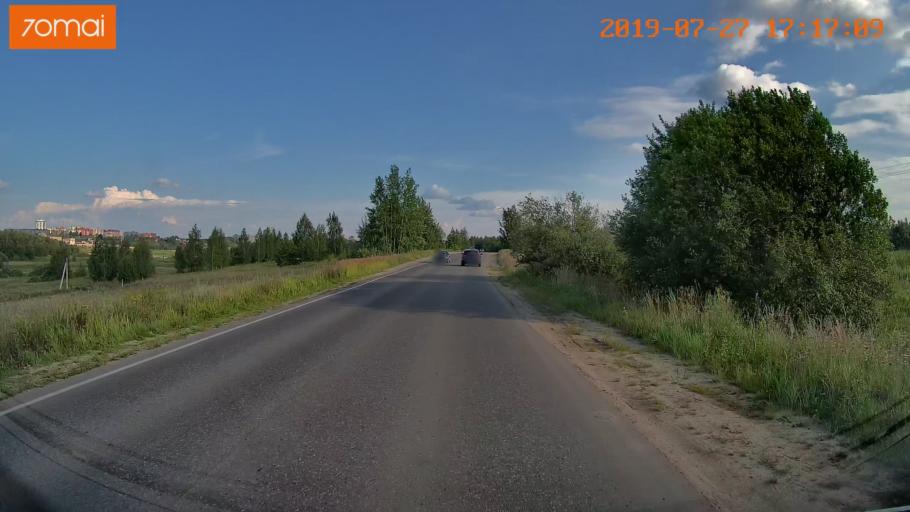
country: RU
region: Ivanovo
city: Novo-Talitsy
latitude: 57.0398
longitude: 40.8922
